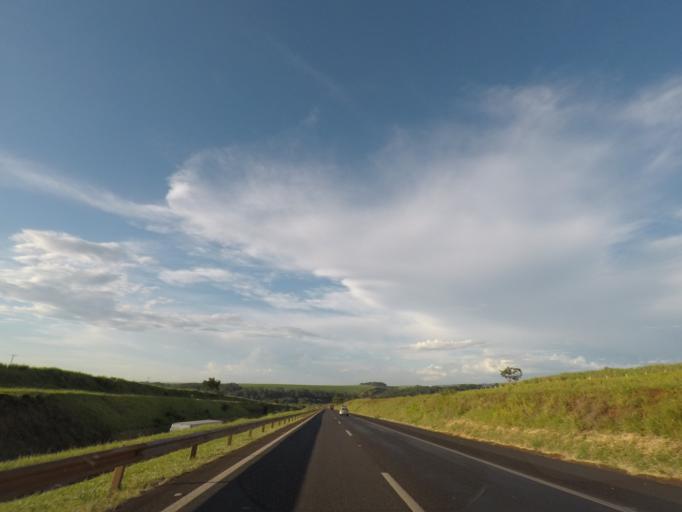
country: BR
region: Sao Paulo
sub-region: Ituverava
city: Ituverava
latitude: -20.2673
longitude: -47.7987
